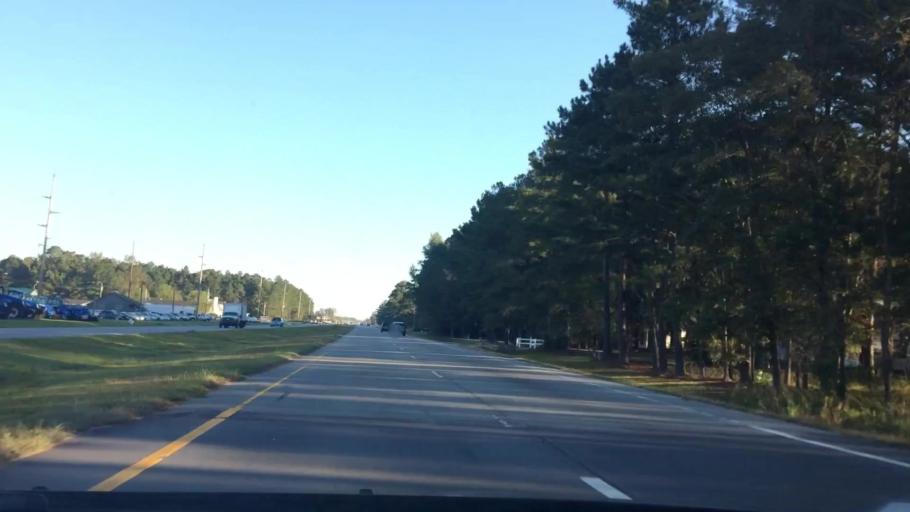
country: US
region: North Carolina
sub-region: Pitt County
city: Grifton
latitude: 35.4120
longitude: -77.4349
